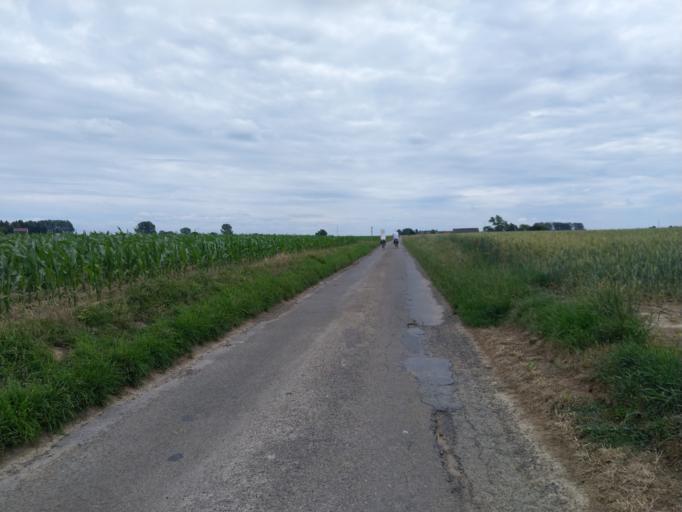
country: BE
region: Wallonia
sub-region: Province du Hainaut
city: Chievres
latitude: 50.5387
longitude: 3.8175
